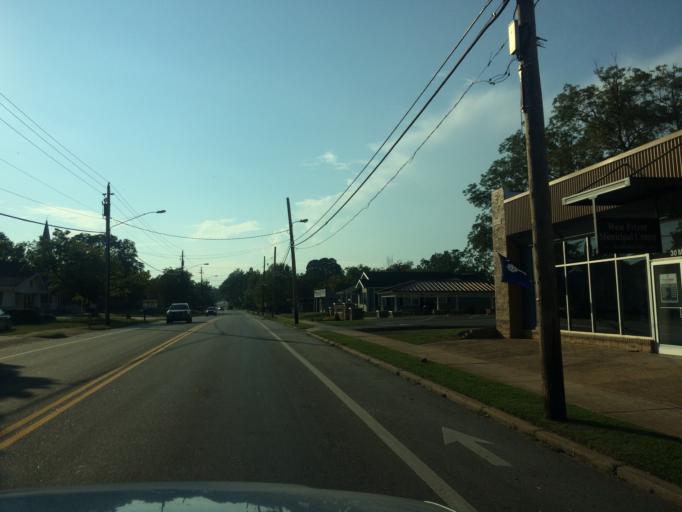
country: US
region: South Carolina
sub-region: Anderson County
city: Williamston
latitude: 34.6445
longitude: -82.4683
